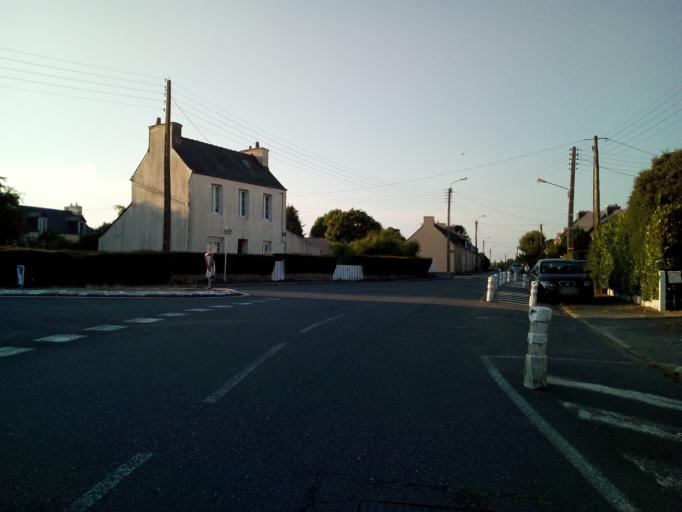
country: FR
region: Brittany
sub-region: Departement du Finistere
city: Landivisiau
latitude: 48.5017
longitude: -4.0784
